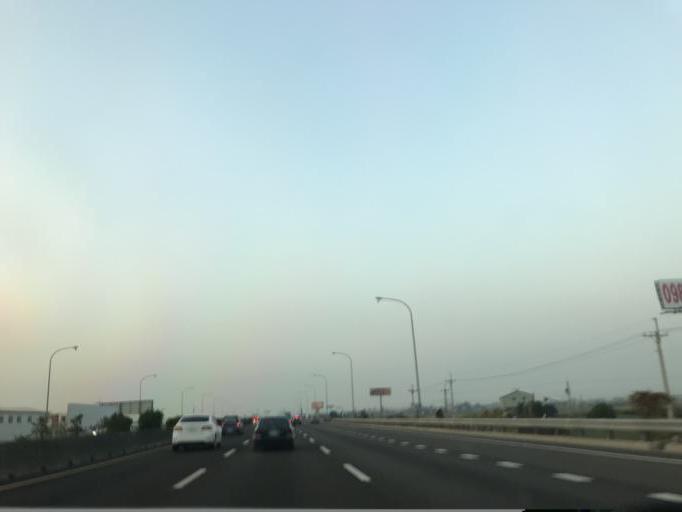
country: TW
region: Taiwan
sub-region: Yunlin
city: Douliu
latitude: 23.7281
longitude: 120.4733
